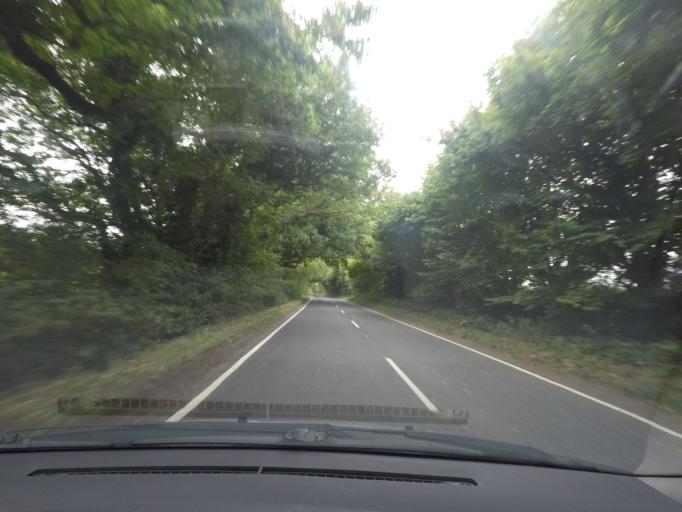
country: GB
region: England
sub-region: Wiltshire
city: Marlborough
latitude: 51.4004
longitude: -1.7496
